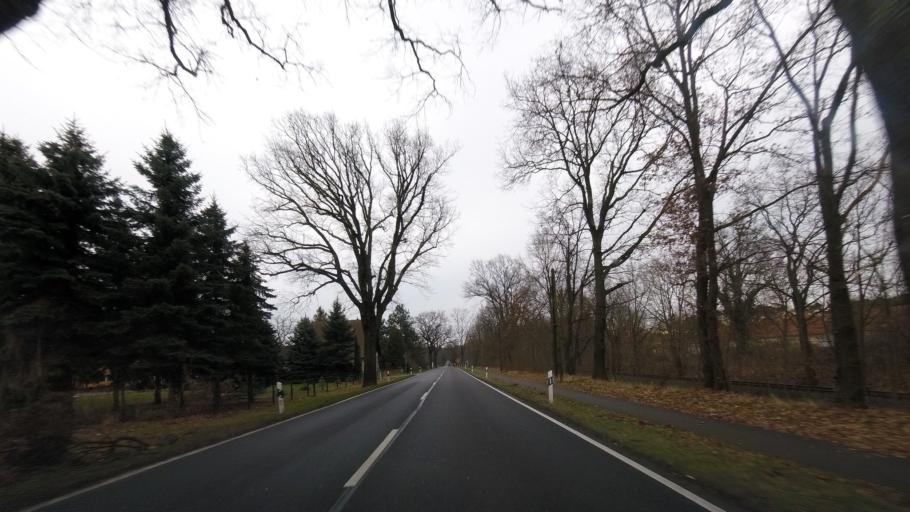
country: DE
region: Brandenburg
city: Treuenbrietzen
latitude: 52.0832
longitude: 12.8794
